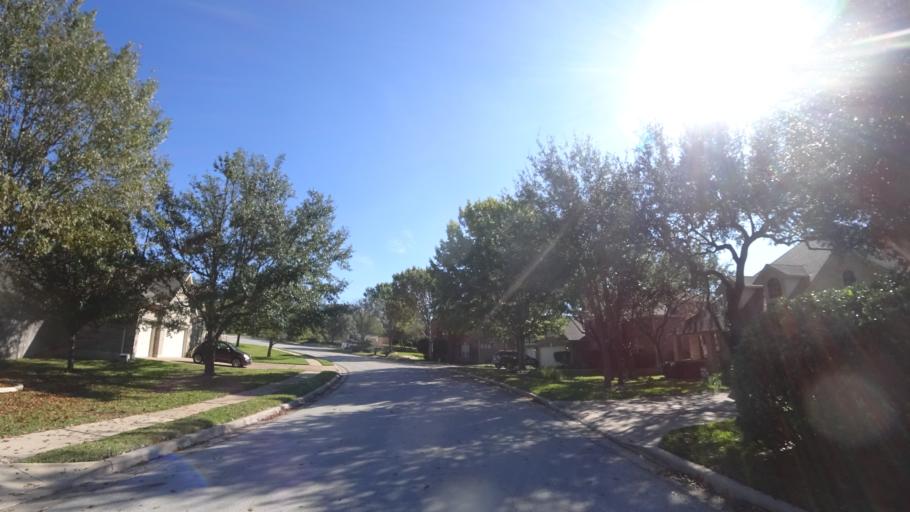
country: US
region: Texas
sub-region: Travis County
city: Hudson Bend
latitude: 30.3749
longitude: -97.8994
